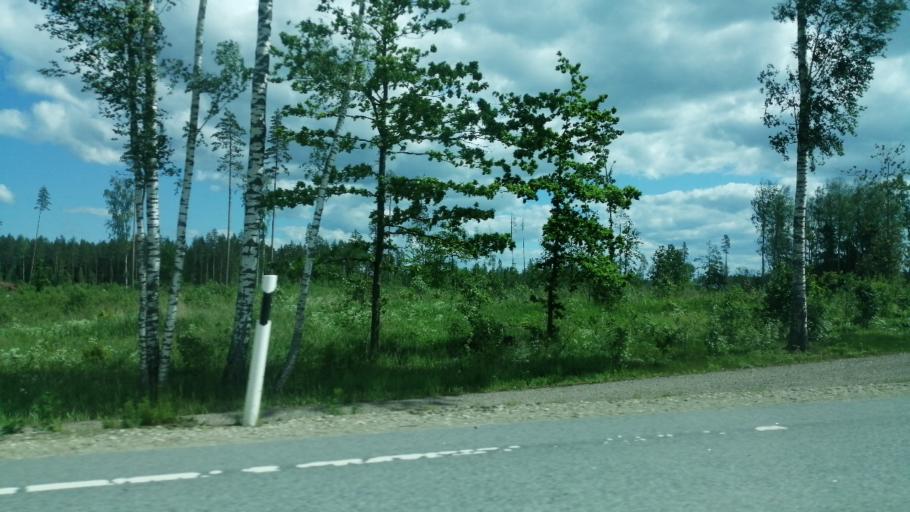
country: EE
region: Polvamaa
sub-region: Polva linn
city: Polva
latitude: 58.0591
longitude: 27.0100
